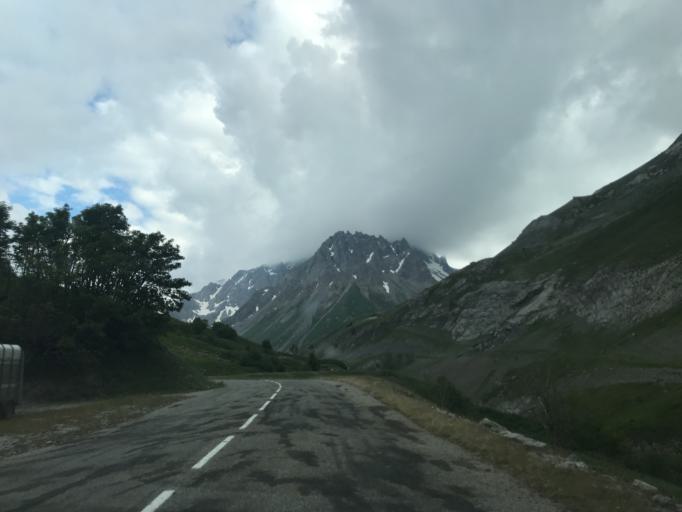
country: FR
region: Rhone-Alpes
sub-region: Departement de la Savoie
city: Valloire
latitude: 45.0978
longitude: 6.4298
